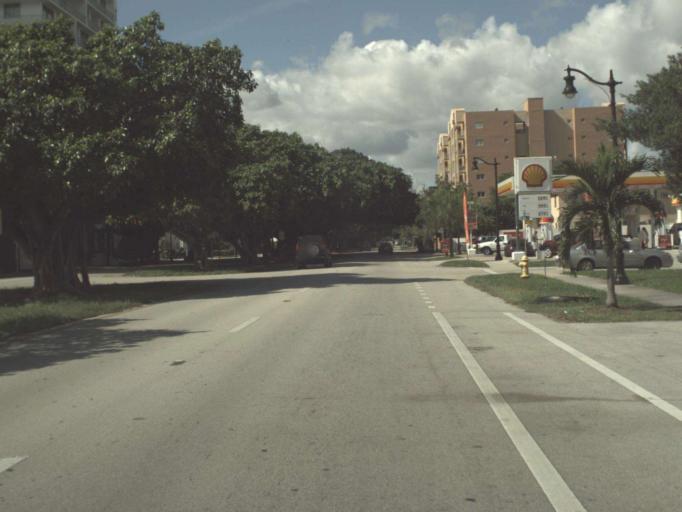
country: US
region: Florida
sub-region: Miami-Dade County
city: Miami
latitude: 25.7592
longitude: -80.2029
